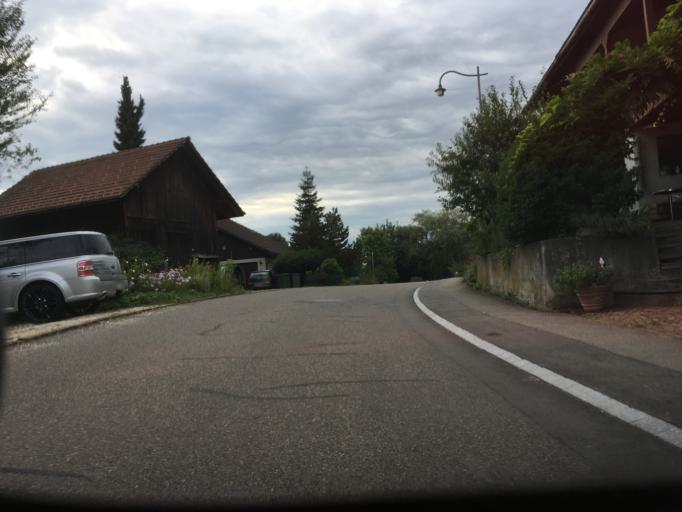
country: CH
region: Zurich
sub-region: Bezirk Pfaeffikon
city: Hittnau / Hittnau (Dorf)
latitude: 47.3767
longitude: 8.8152
